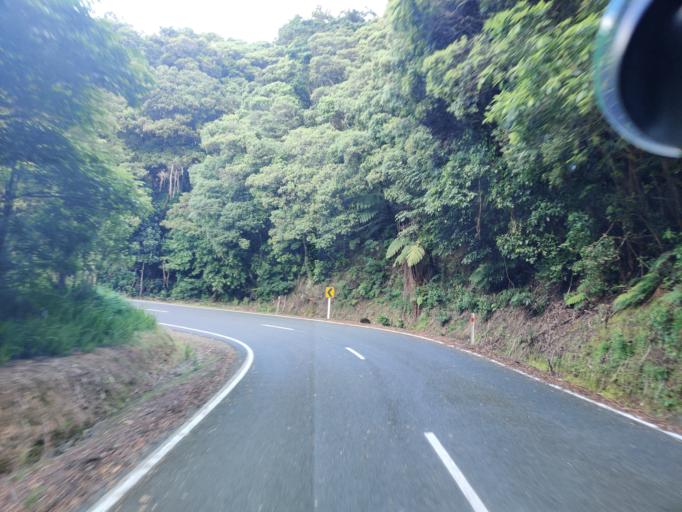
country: NZ
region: Northland
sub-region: Whangarei
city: Ngunguru
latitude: -35.5779
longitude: 174.4119
